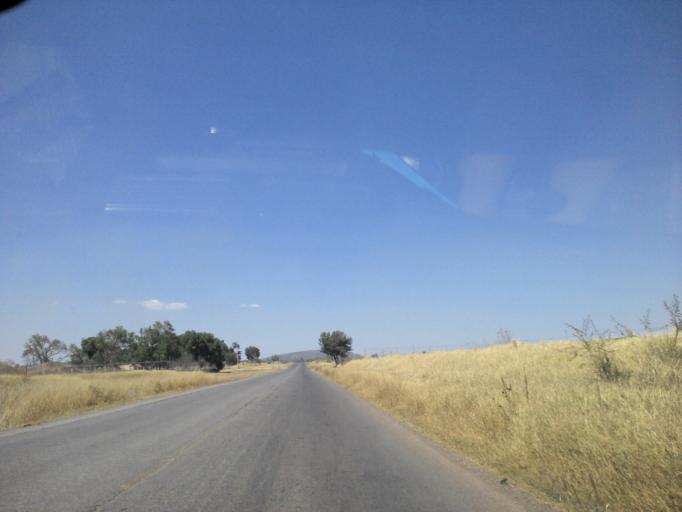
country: MX
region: Jalisco
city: Tepatitlan de Morelos
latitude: 20.8387
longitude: -102.7226
